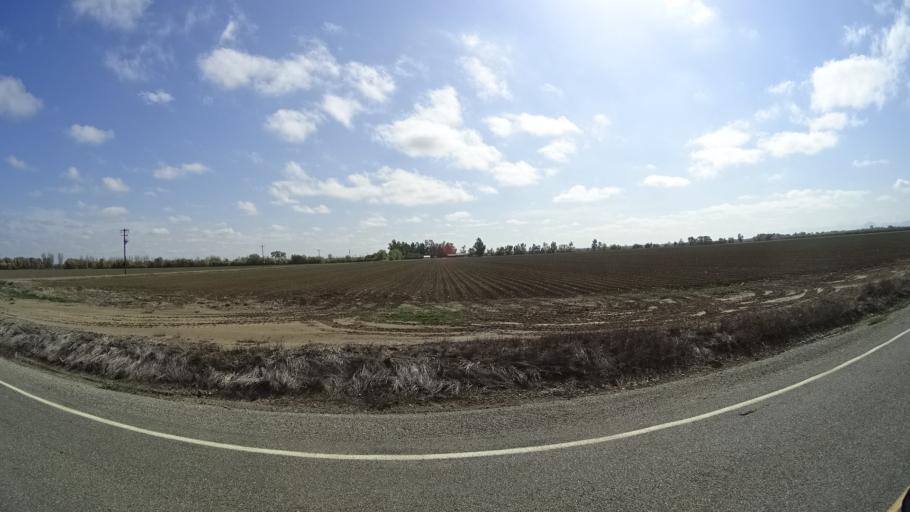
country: US
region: California
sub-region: Butte County
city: Biggs
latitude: 39.4196
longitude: -121.9295
